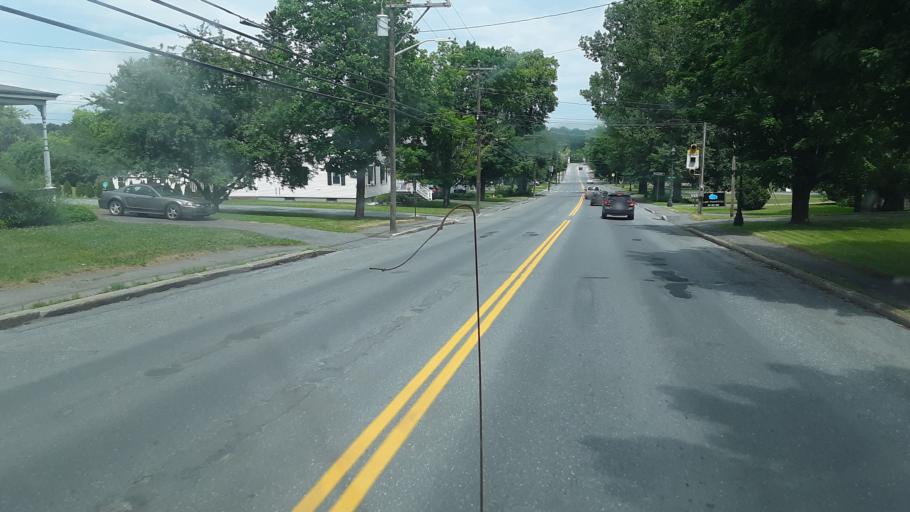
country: US
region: Maine
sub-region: Aroostook County
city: Fort Fairfield
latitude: 46.7696
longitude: -67.8412
